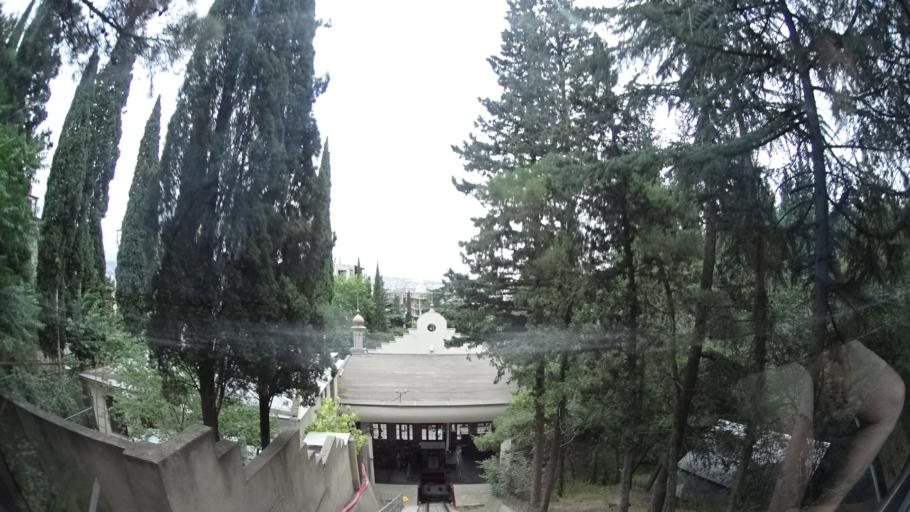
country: GE
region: T'bilisi
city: Tbilisi
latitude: 41.6954
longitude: 44.7914
